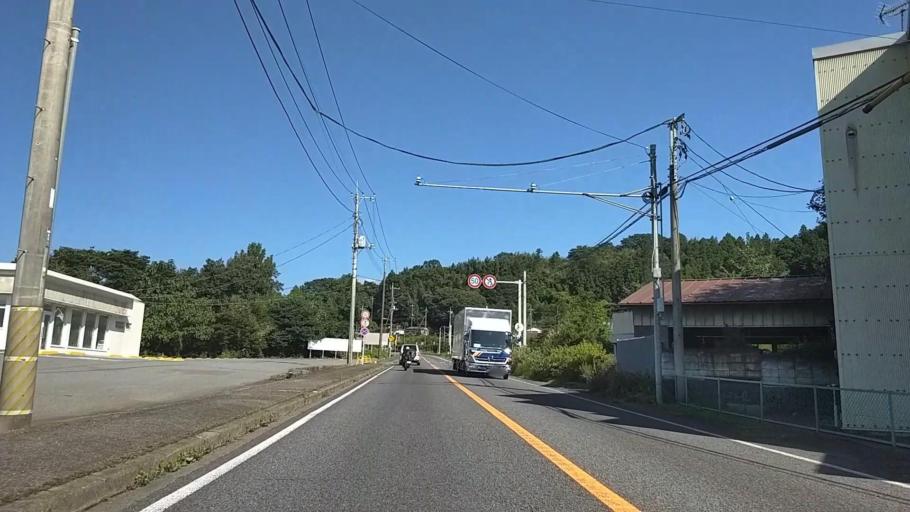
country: JP
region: Gunma
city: Annaka
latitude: 36.3229
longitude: 138.7676
